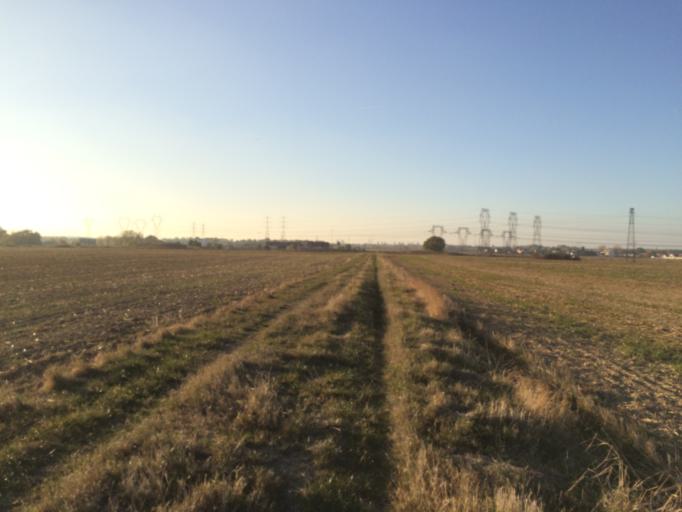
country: FR
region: Ile-de-France
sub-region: Departement de l'Essonne
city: Nozay
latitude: 48.6638
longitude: 2.2227
